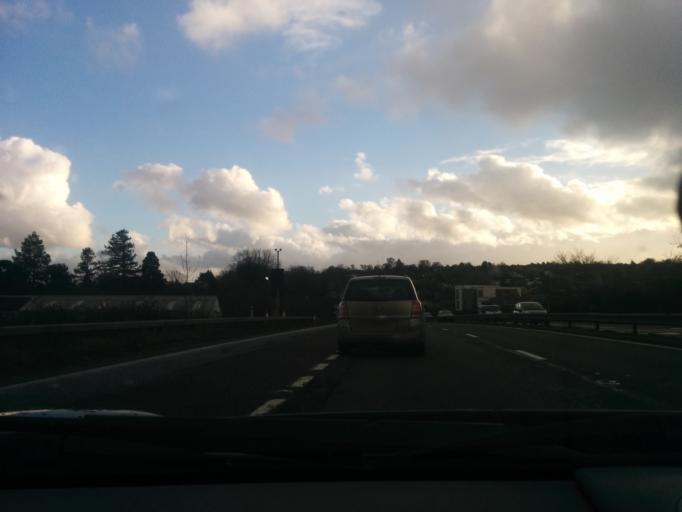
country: GB
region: England
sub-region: Oxfordshire
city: Boars Hill
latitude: 51.7525
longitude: -1.2964
